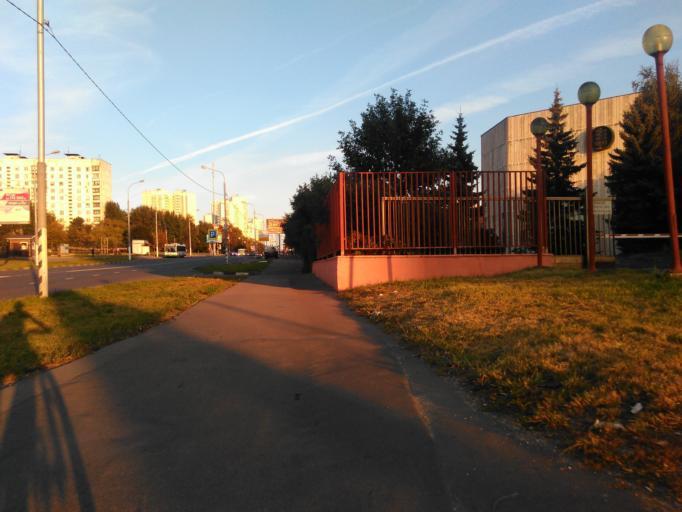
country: RU
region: Moscow
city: Troparevo
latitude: 55.6491
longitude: 37.5105
